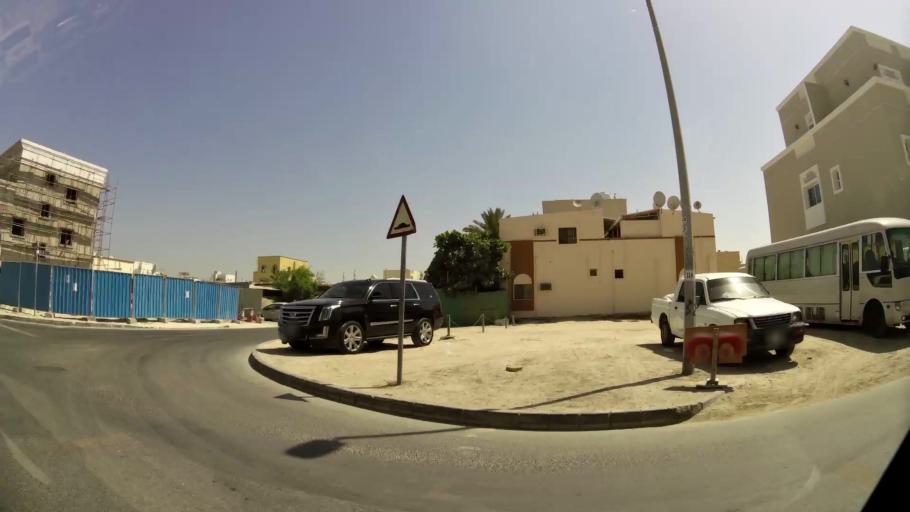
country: AE
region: Ash Shariqah
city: Sharjah
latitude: 25.2268
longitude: 55.2762
